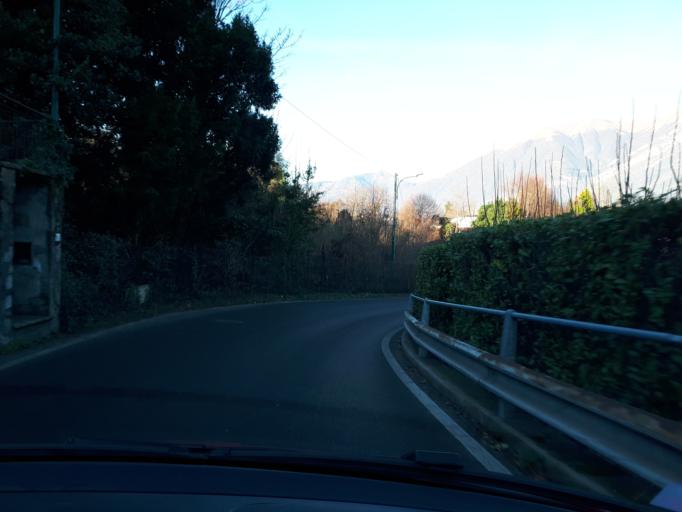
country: IT
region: Lombardy
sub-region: Provincia di Como
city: Bellagio
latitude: 45.9726
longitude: 9.2617
